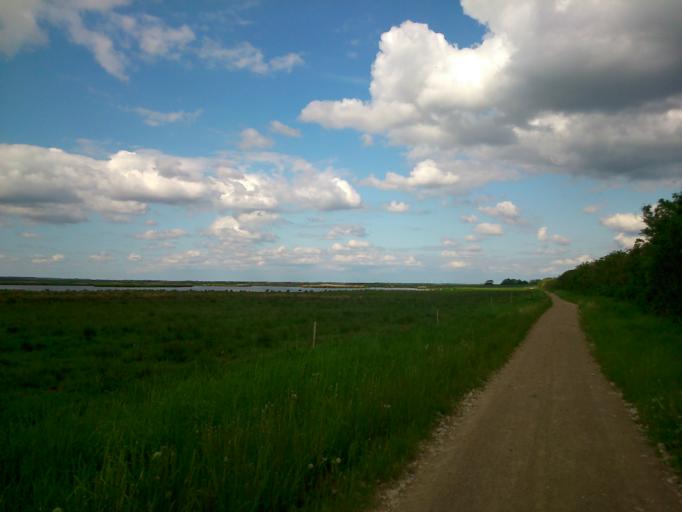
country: DK
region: Central Jutland
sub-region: Ringkobing-Skjern Kommune
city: Skjern
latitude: 55.9032
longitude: 8.4262
